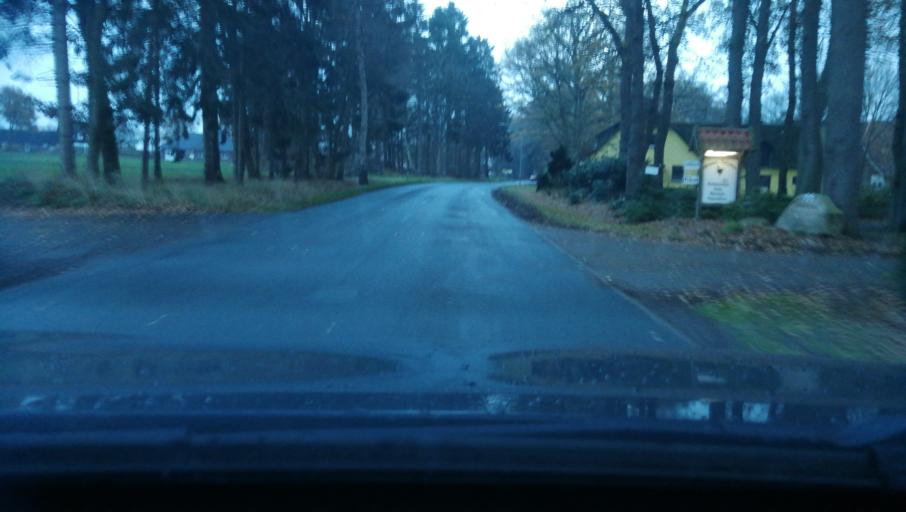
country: DE
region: Lower Saxony
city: Fintel
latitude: 53.1411
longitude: 9.6957
